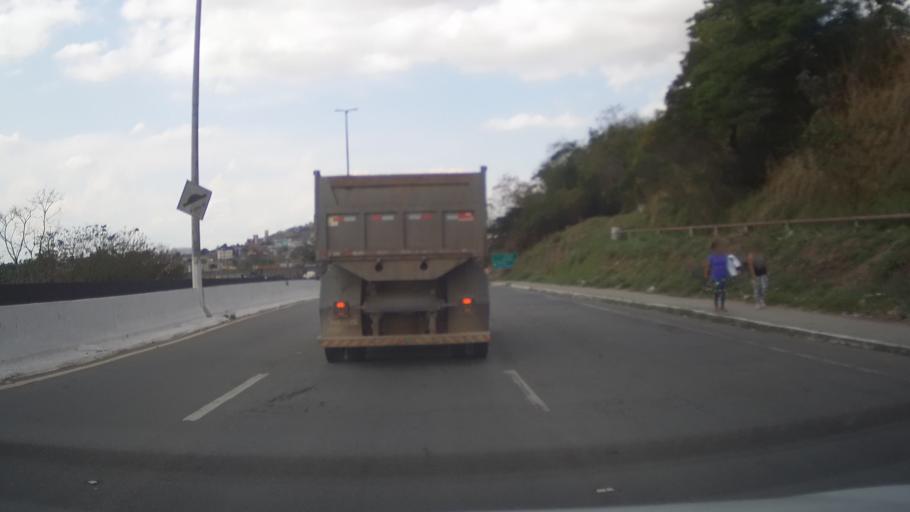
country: BR
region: Minas Gerais
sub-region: Belo Horizonte
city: Belo Horizonte
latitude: -19.8622
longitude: -43.8934
